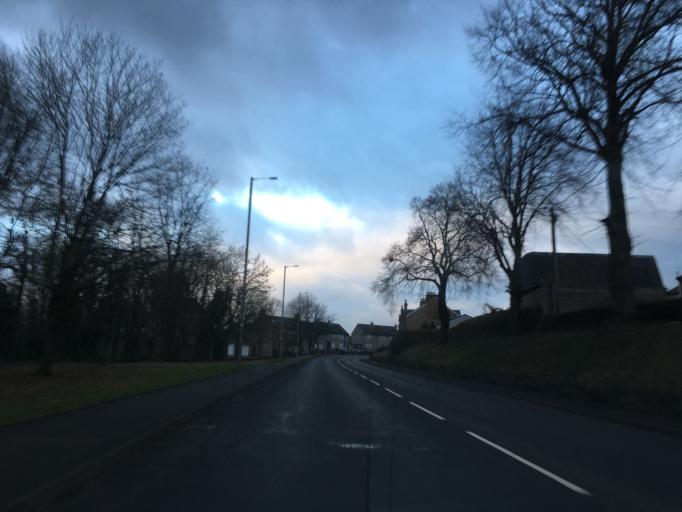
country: GB
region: Scotland
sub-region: Stirling
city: Bannockburn
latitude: 56.0928
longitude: -3.9177
